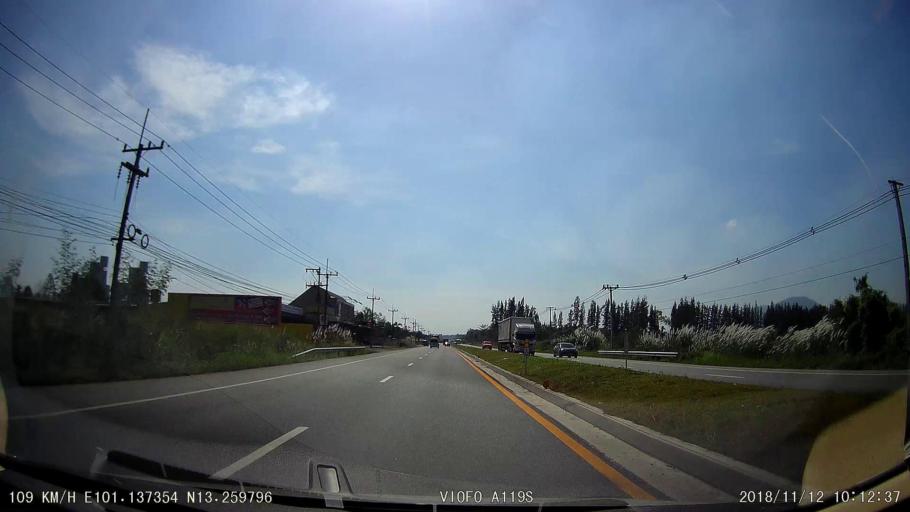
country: TH
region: Chon Buri
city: Ban Bueng
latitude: 13.2597
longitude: 101.1373
